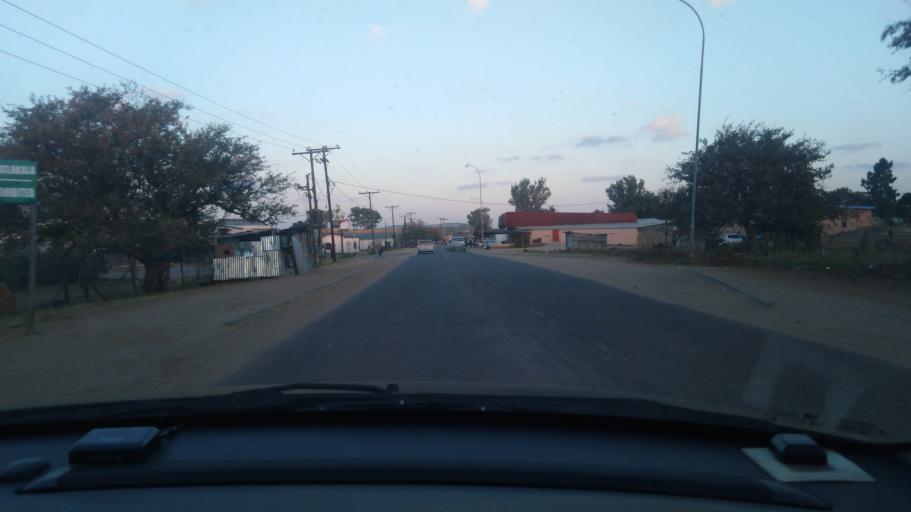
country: BW
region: Central
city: Mahalapye
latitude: -23.1045
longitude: 26.8311
